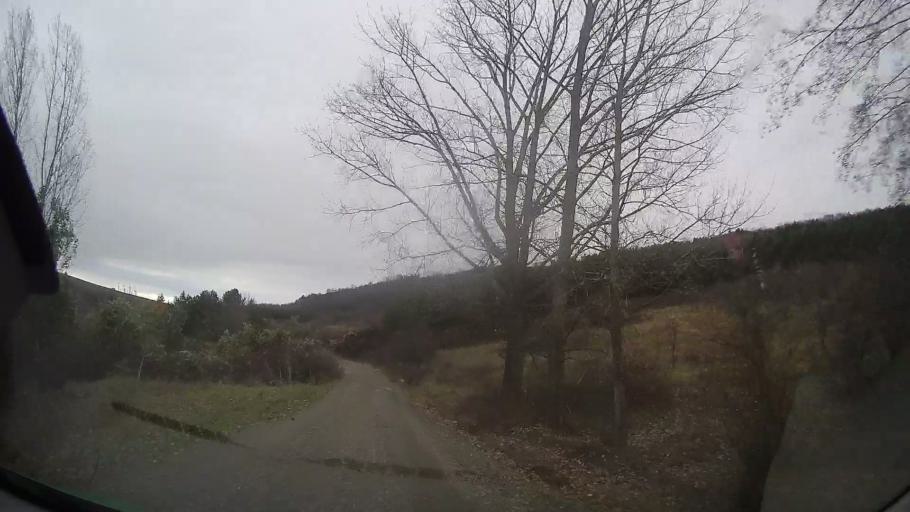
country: RO
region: Mures
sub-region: Comuna Bala
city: Bala
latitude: 46.6794
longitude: 24.4864
